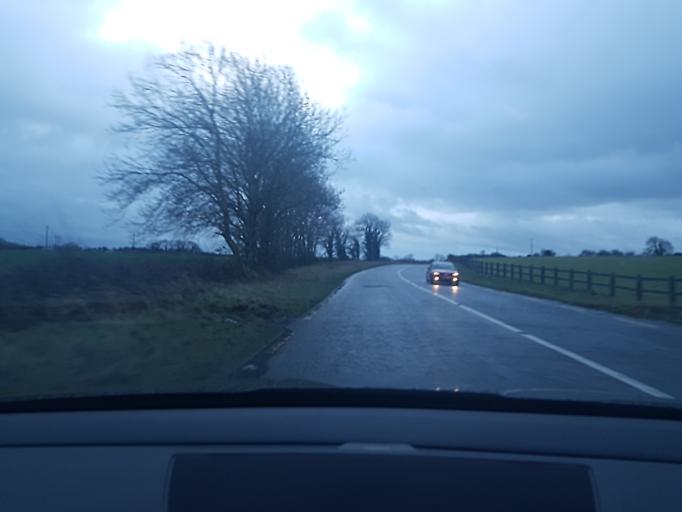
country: IE
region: Connaught
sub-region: County Galway
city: Tuam
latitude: 53.5368
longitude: -8.8834
